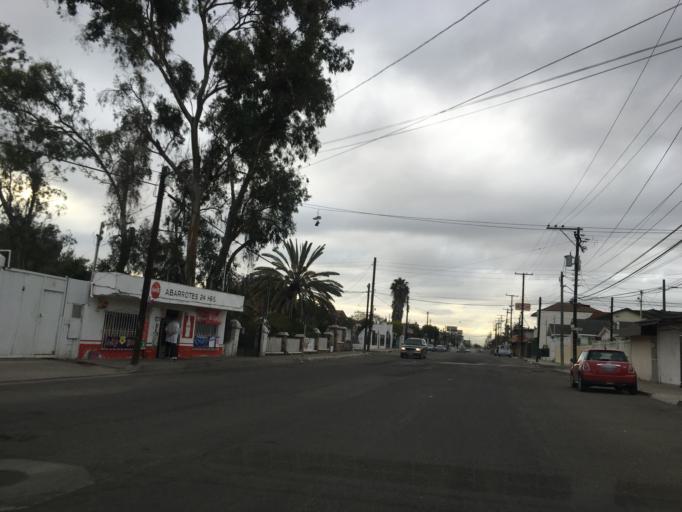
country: MX
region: Baja California
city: Tijuana
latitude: 32.5385
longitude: -117.0591
